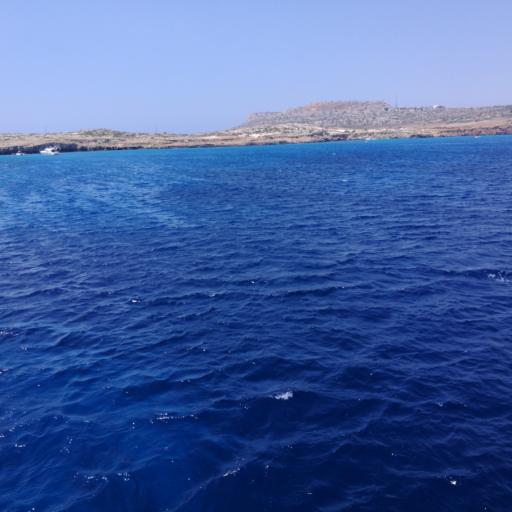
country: CY
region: Ammochostos
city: Protaras
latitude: 34.9675
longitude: 34.0853
